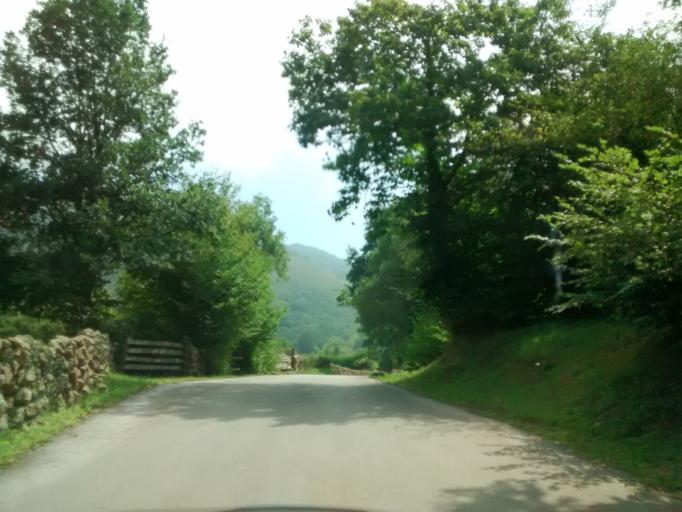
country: ES
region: Cantabria
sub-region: Provincia de Cantabria
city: Ruente
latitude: 43.2512
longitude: -4.2448
